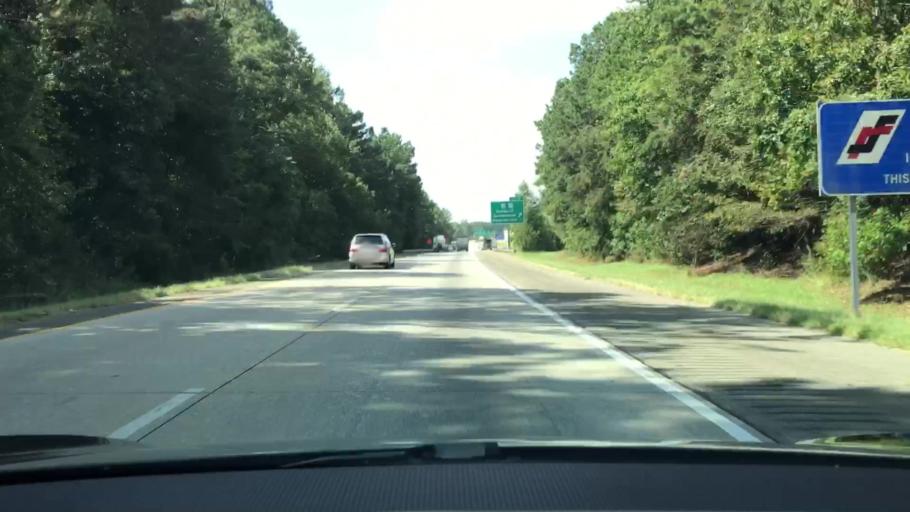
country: US
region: Georgia
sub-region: Hall County
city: Oakwood
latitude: 34.2357
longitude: -83.8457
